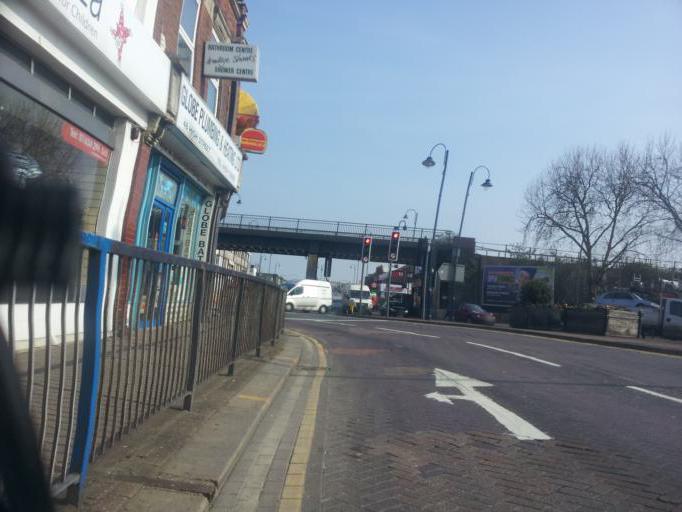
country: GB
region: England
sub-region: Kent
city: Strood
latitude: 51.3950
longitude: 0.4965
